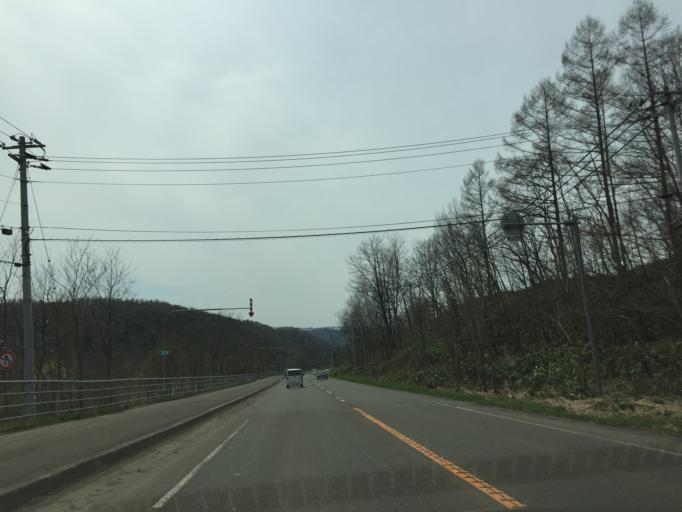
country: JP
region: Hokkaido
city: Ashibetsu
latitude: 43.5525
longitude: 142.1789
